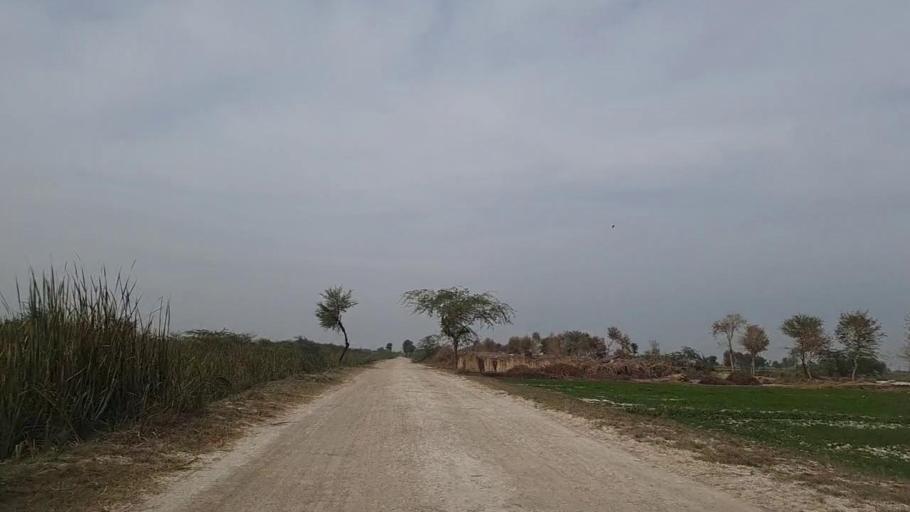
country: PK
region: Sindh
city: Daur
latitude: 26.4183
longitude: 68.4231
